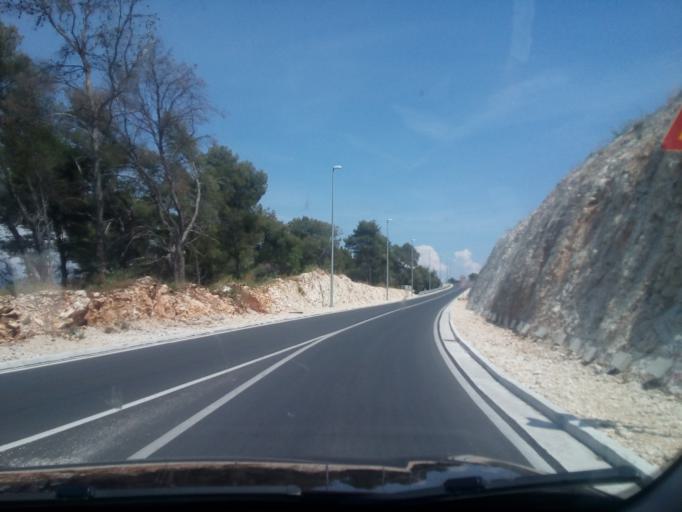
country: HR
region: Splitsko-Dalmatinska
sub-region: Grad Trogir
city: Trogir
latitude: 43.5164
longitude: 16.2654
